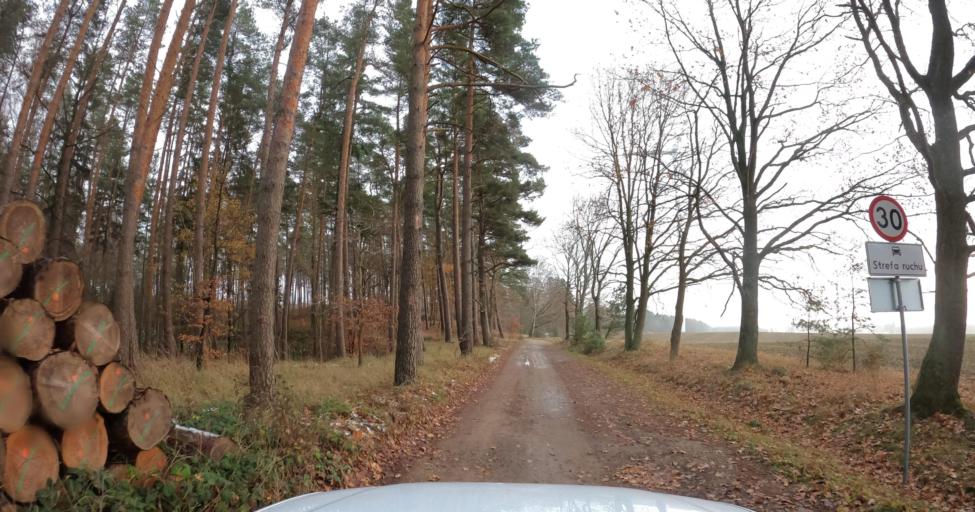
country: PL
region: West Pomeranian Voivodeship
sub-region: Powiat bialogardzki
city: Karlino
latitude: 53.9262
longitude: 15.8361
